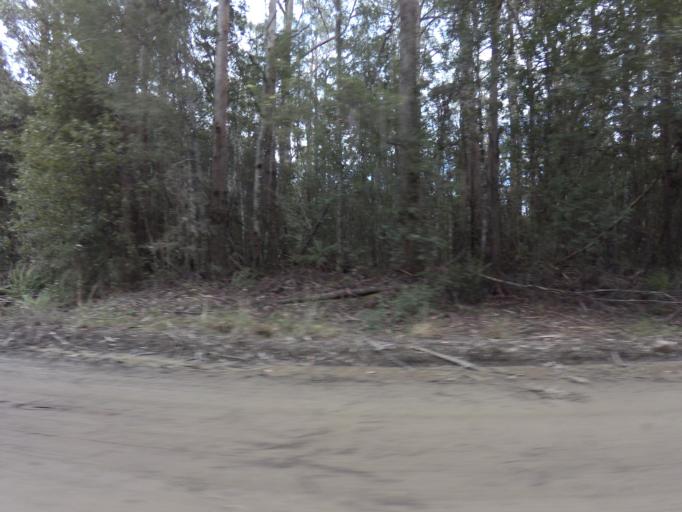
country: AU
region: Tasmania
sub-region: Huon Valley
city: Geeveston
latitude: -43.4963
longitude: 146.8799
